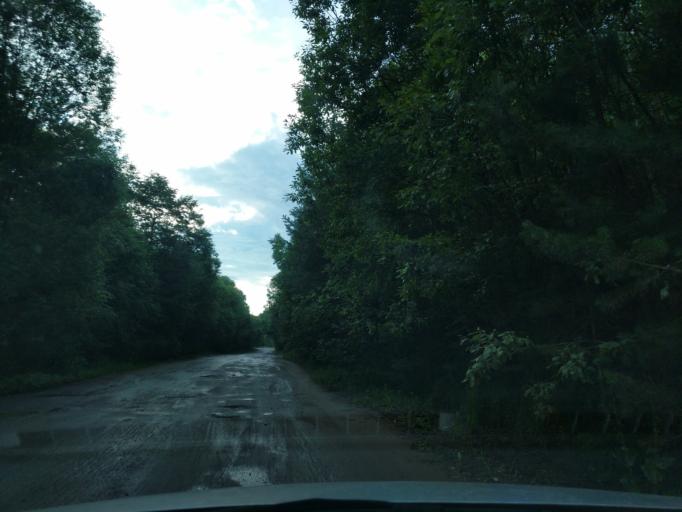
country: RU
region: Kaluga
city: Myatlevo
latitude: 54.8465
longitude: 35.6151
